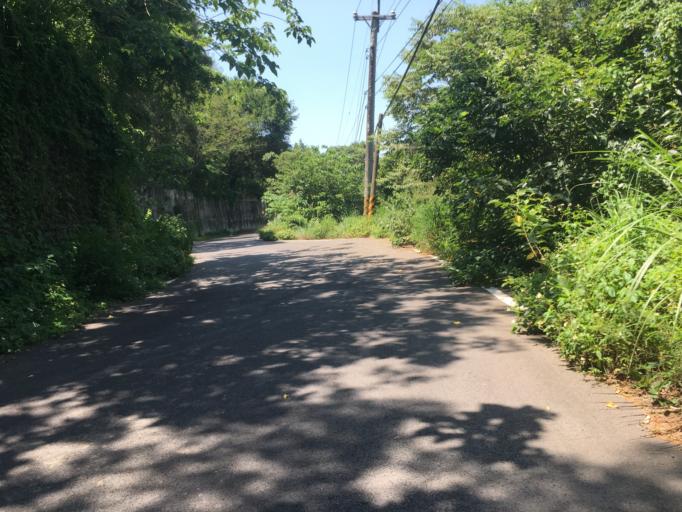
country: TW
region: Taiwan
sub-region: Hsinchu
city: Hsinchu
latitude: 24.7340
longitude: 120.9801
